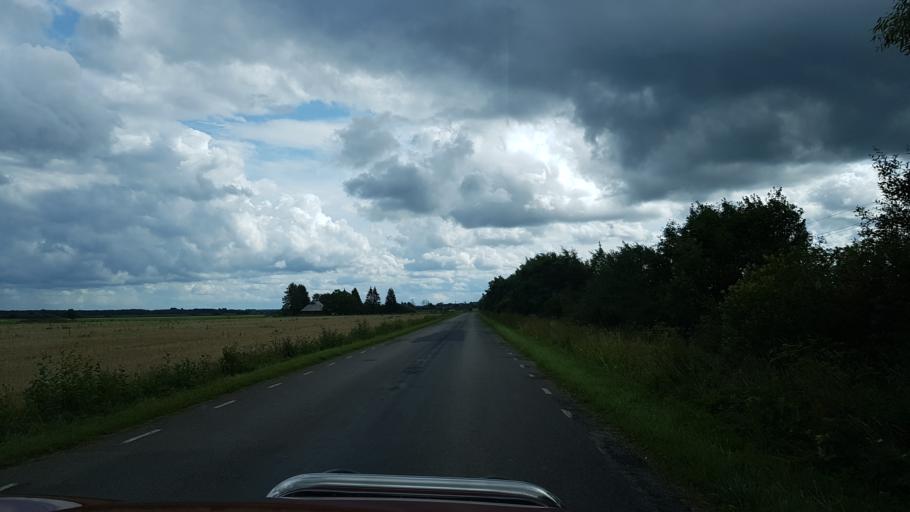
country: EE
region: Laeaene
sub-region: Lihula vald
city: Lihula
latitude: 58.7197
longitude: 23.9785
